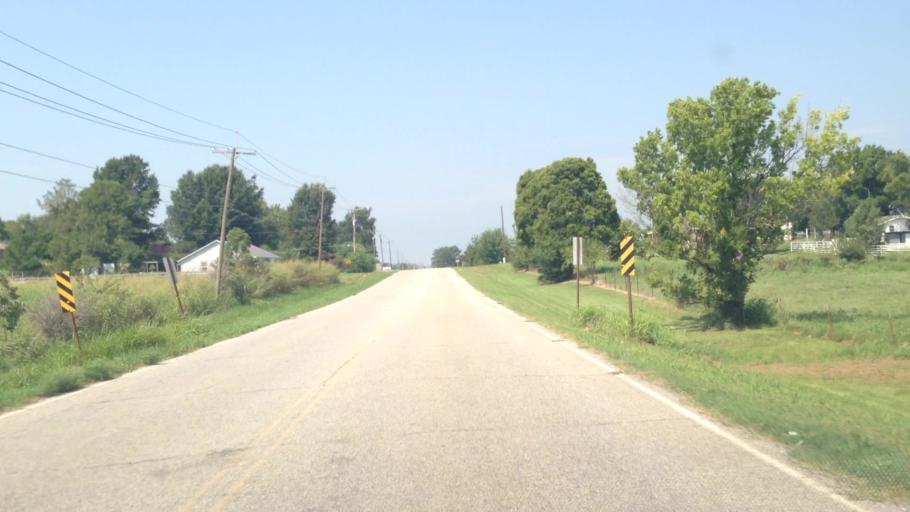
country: US
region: Oklahoma
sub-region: Craig County
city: Vinita
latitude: 36.6560
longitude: -95.1284
